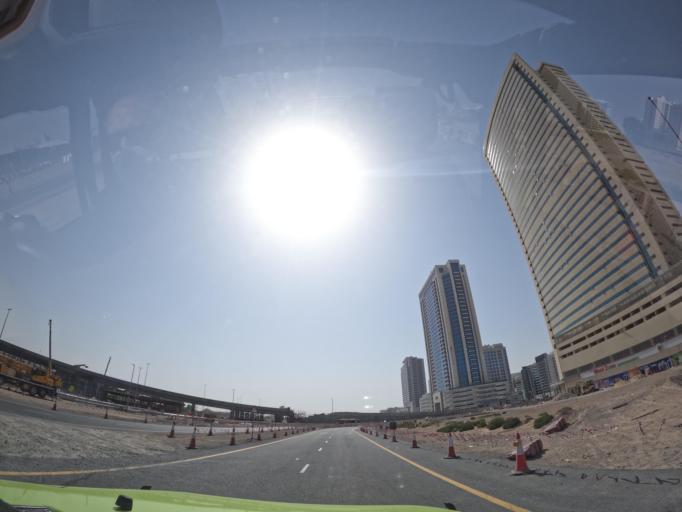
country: AE
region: Dubai
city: Dubai
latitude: 25.0964
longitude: 55.3834
